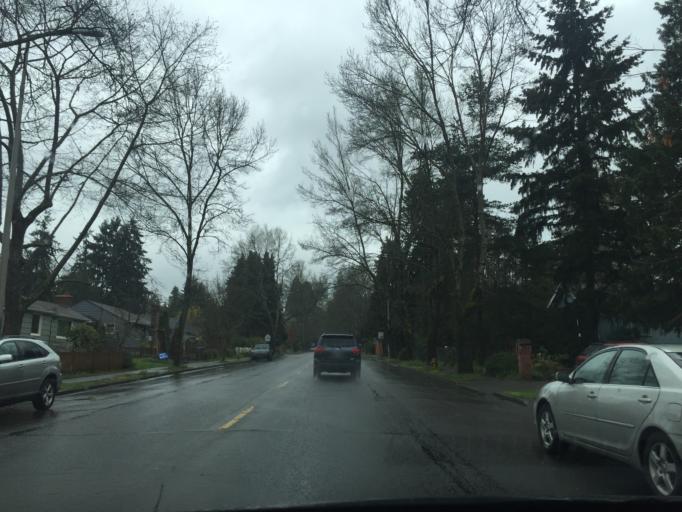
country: US
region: Washington
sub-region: King County
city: Lake Forest Park
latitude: 47.7090
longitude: -122.2907
